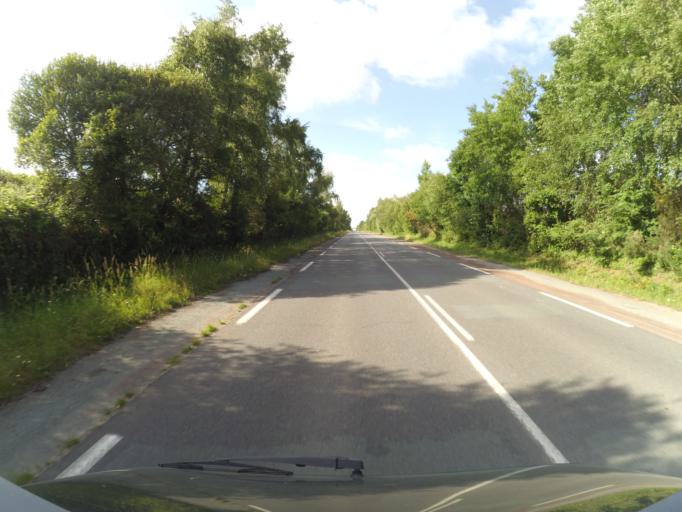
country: FR
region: Poitou-Charentes
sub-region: Departement de la Charente-Maritime
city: Le Gua
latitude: 45.7787
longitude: -0.9362
